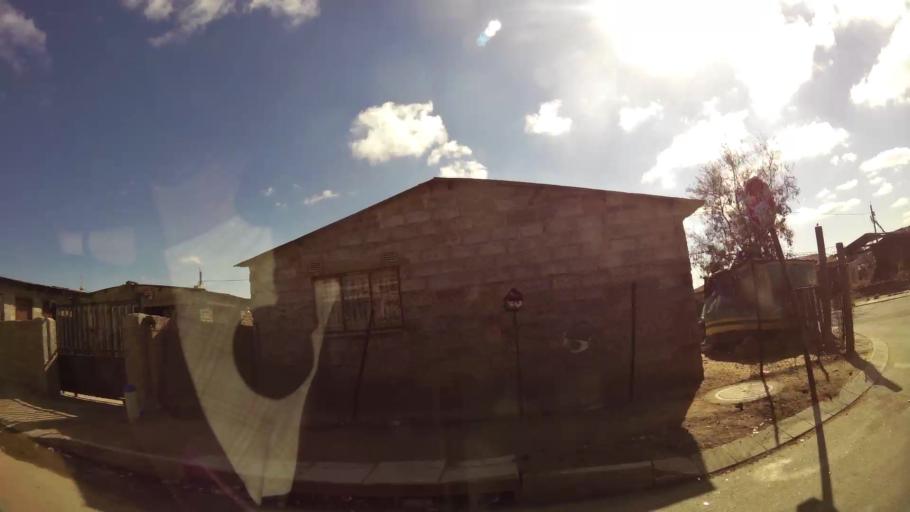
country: ZA
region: Gauteng
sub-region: City of Johannesburg Metropolitan Municipality
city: Modderfontein
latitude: -26.0420
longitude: 28.1794
